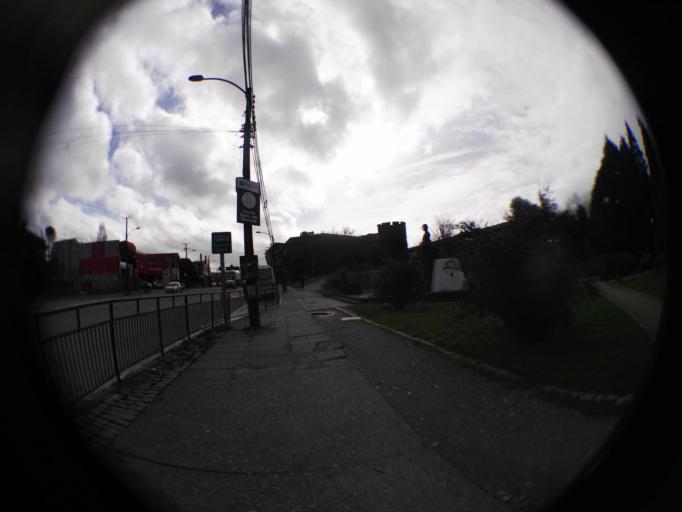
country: CL
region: Los Rios
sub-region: Provincia de Valdivia
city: Valdivia
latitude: -39.8183
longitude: -73.2321
